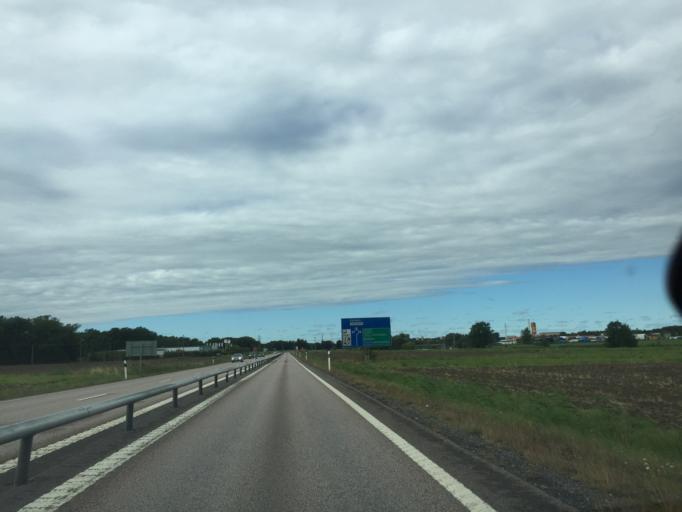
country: SE
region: Vaestmanland
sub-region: Arboga Kommun
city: Arboga
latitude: 59.3974
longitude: 15.8997
